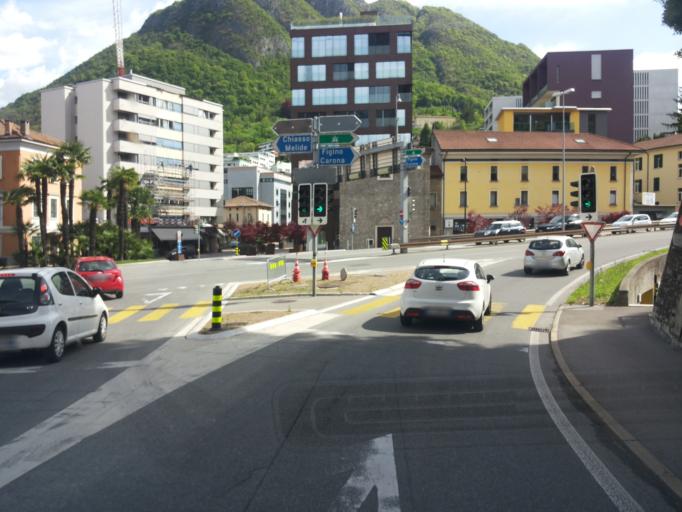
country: CH
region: Ticino
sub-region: Lugano District
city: Sorengo
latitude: 45.9919
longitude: 8.9428
